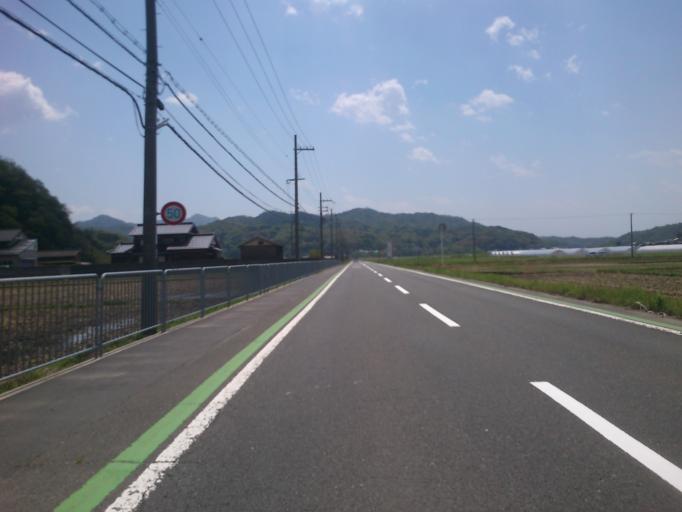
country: JP
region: Kyoto
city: Miyazu
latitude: 35.7236
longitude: 135.1071
